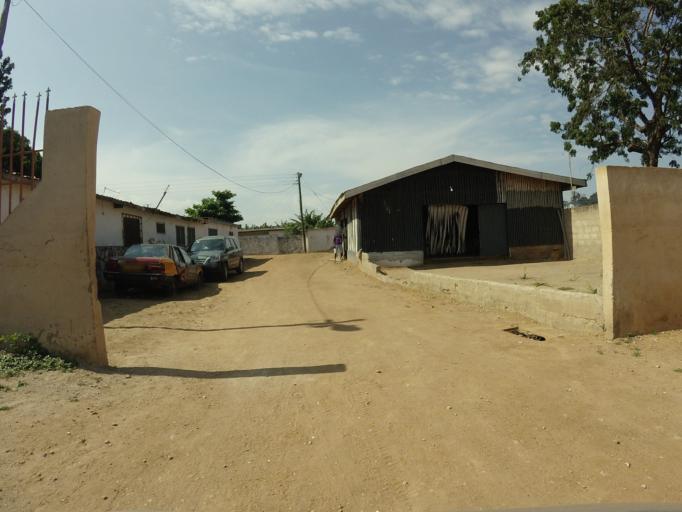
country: GH
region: Greater Accra
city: Dome
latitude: 5.6250
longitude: -0.2292
